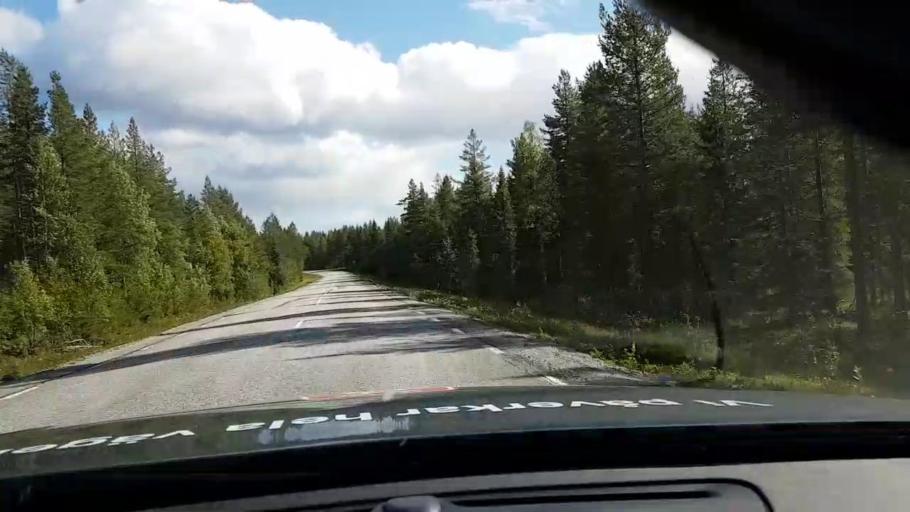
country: SE
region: Vaesternorrland
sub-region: OErnskoeldsviks Kommun
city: Bredbyn
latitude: 63.7610
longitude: 17.6923
